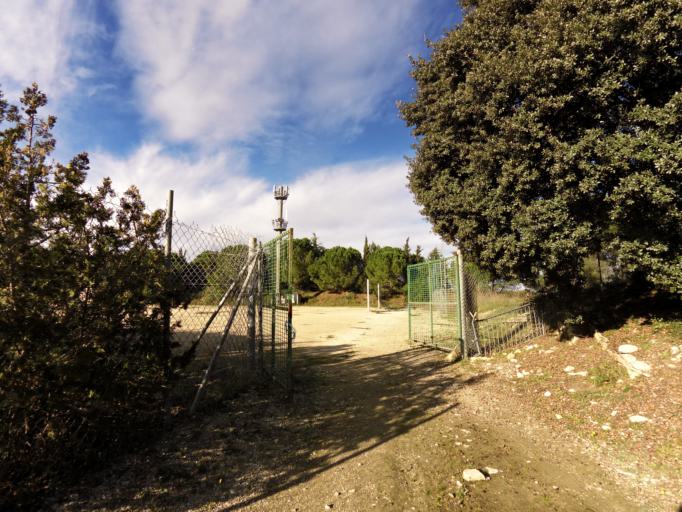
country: FR
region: Languedoc-Roussillon
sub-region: Departement du Gard
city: Langlade
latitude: 43.7991
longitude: 4.2400
